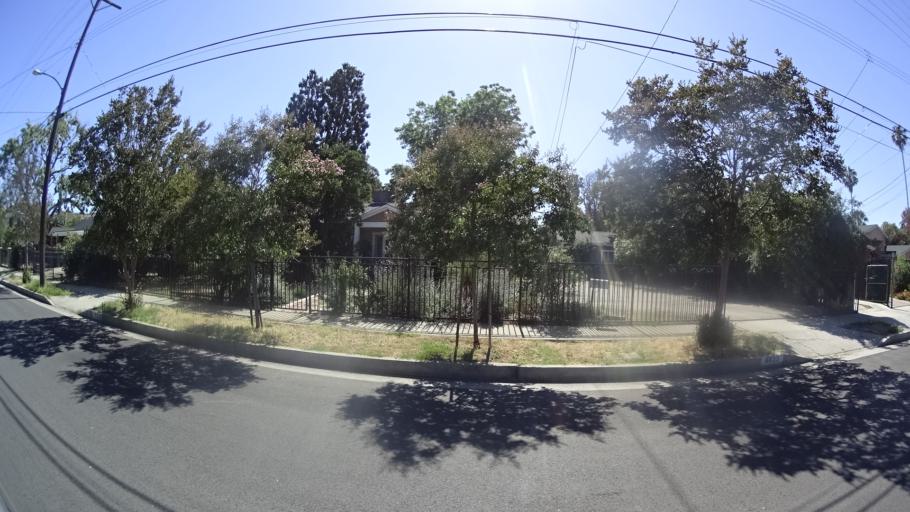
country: US
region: California
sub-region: Los Angeles County
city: Van Nuys
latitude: 34.1913
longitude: -118.4793
